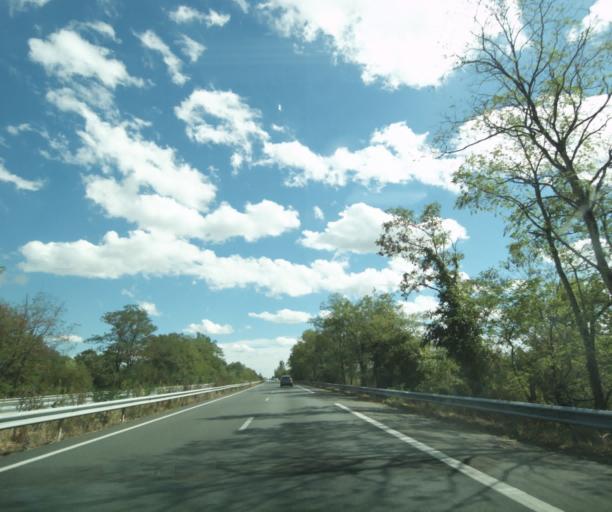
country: FR
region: Aquitaine
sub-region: Departement du Lot-et-Garonne
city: Fourques-sur-Garonne
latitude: 44.4507
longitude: 0.0919
